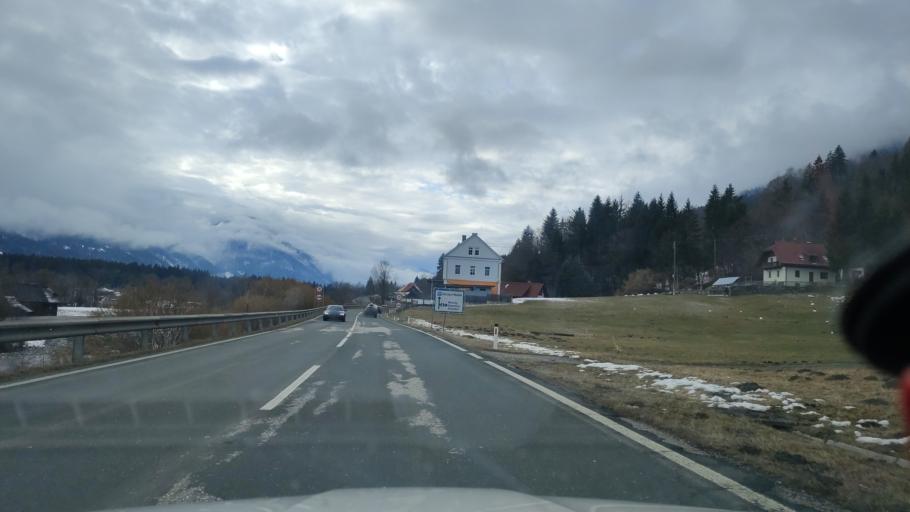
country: AT
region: Carinthia
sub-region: Politischer Bezirk Hermagor
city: Hermagor
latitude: 46.6219
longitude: 13.3147
